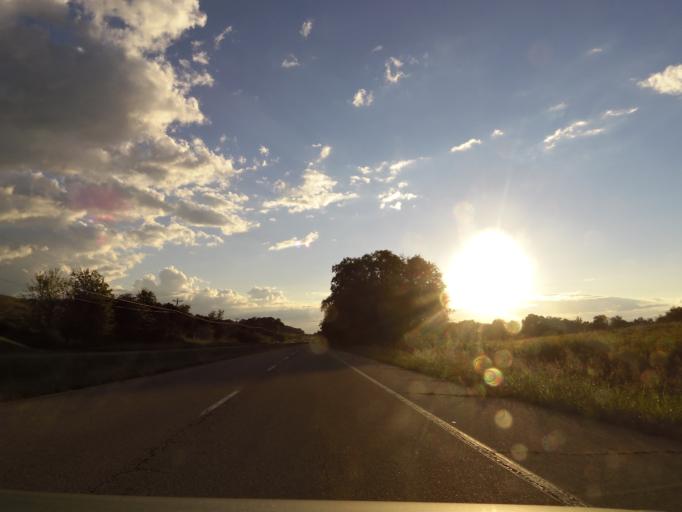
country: US
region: Tennessee
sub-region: Jefferson County
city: New Market
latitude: 36.0900
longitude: -83.5895
